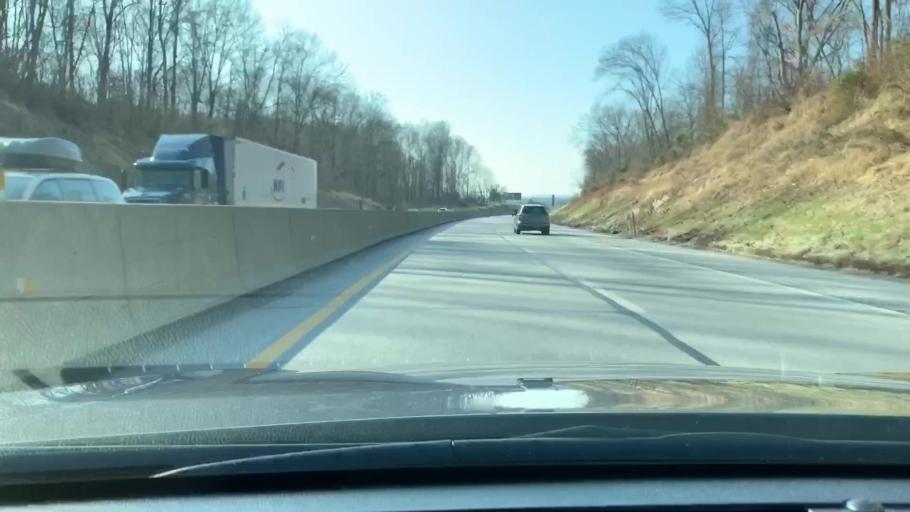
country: US
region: Pennsylvania
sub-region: Lebanon County
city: Campbelltown
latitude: 40.2124
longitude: -76.5377
